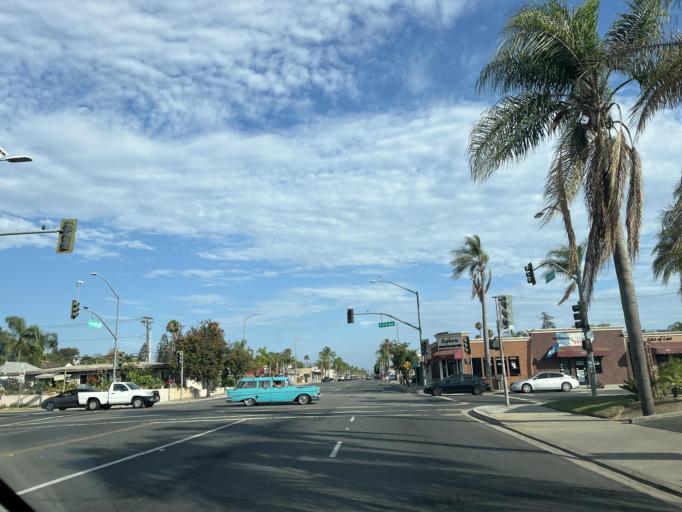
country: US
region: California
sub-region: San Diego County
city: Escondido
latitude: 33.1170
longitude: -117.0817
